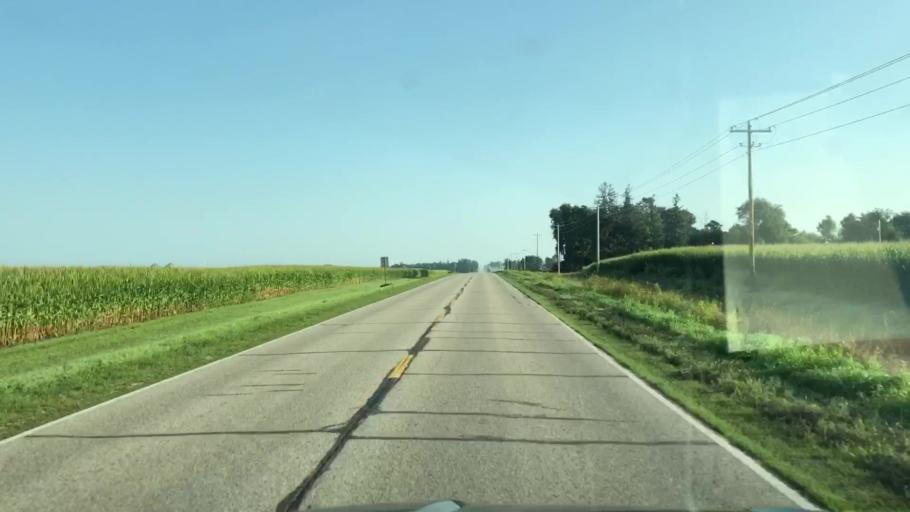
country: US
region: Iowa
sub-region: Lyon County
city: George
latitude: 43.3535
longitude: -95.9984
